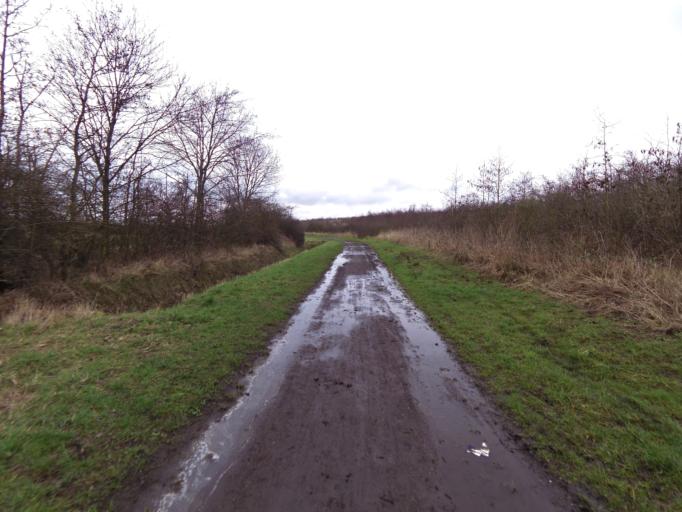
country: GB
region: England
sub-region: Doncaster
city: Bentley
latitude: 53.5633
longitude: -1.1491
